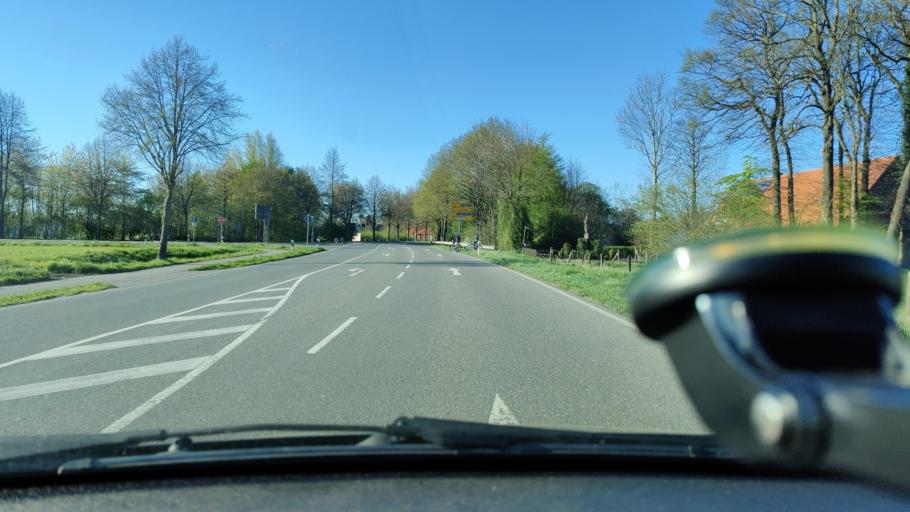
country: DE
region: North Rhine-Westphalia
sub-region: Regierungsbezirk Munster
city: Legden
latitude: 51.9998
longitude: 7.1287
